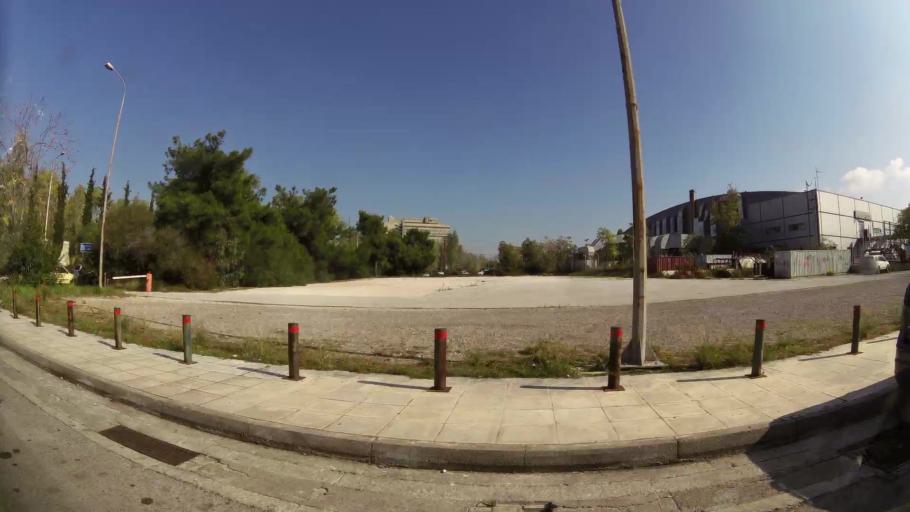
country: GR
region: Attica
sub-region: Nomarchia Athinas
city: Papagou
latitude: 37.9859
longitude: 23.7735
